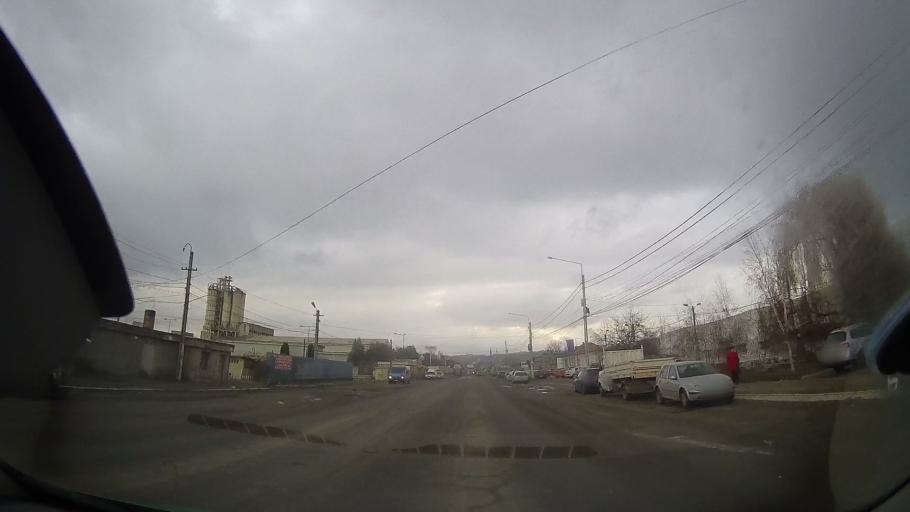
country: RO
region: Cluj
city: Turda
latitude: 46.5539
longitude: 23.7846
